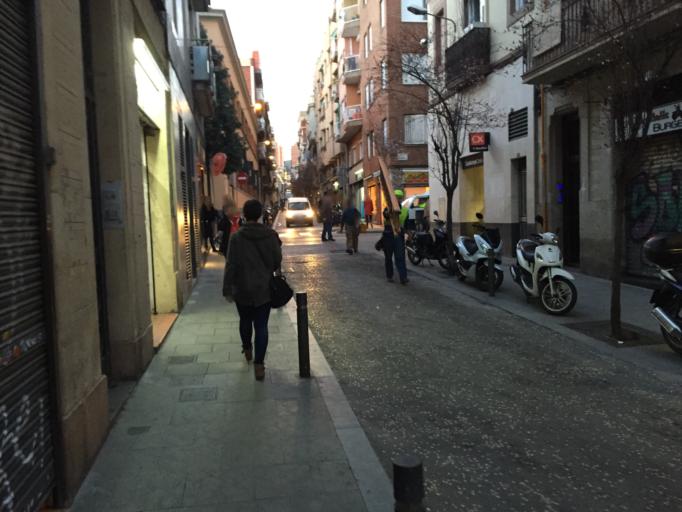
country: ES
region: Catalonia
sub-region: Provincia de Barcelona
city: Gracia
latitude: 41.4052
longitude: 2.1554
